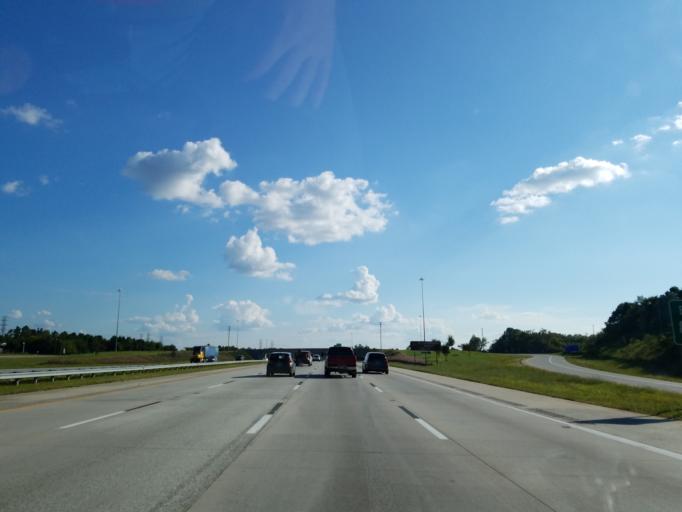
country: US
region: North Carolina
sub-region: Rowan County
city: Spencer
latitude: 35.6985
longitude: -80.4002
